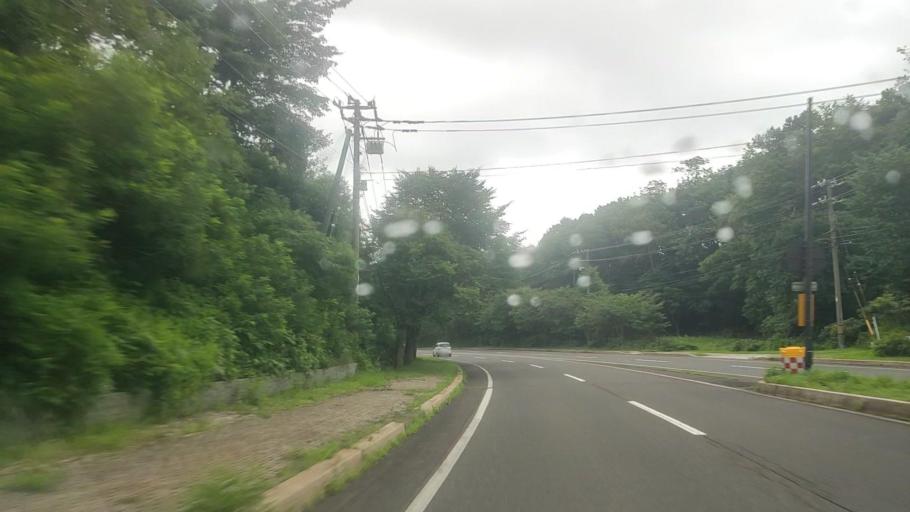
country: JP
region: Hokkaido
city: Shiraoi
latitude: 42.4702
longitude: 141.1494
